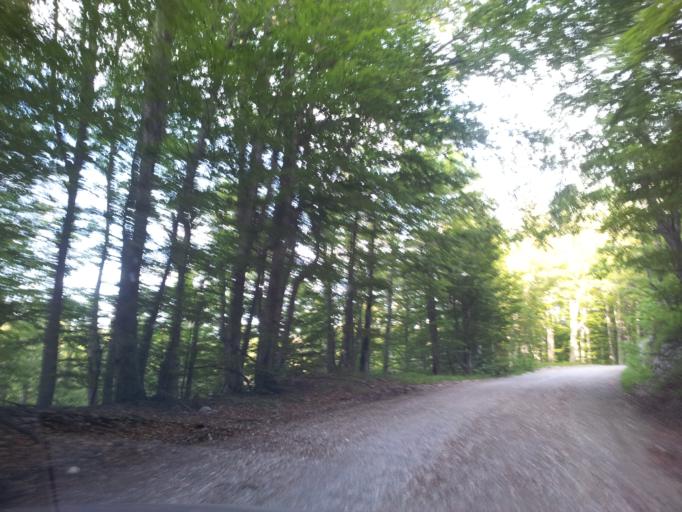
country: HR
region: Zadarska
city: Obrovac
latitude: 44.3013
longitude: 15.6475
